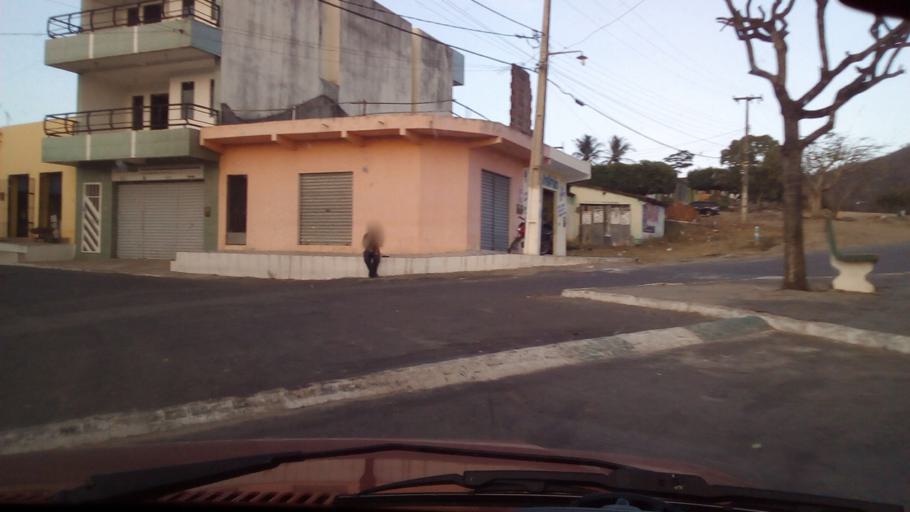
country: BR
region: Paraiba
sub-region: Belem
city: Belem
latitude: -6.7203
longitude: -35.5416
